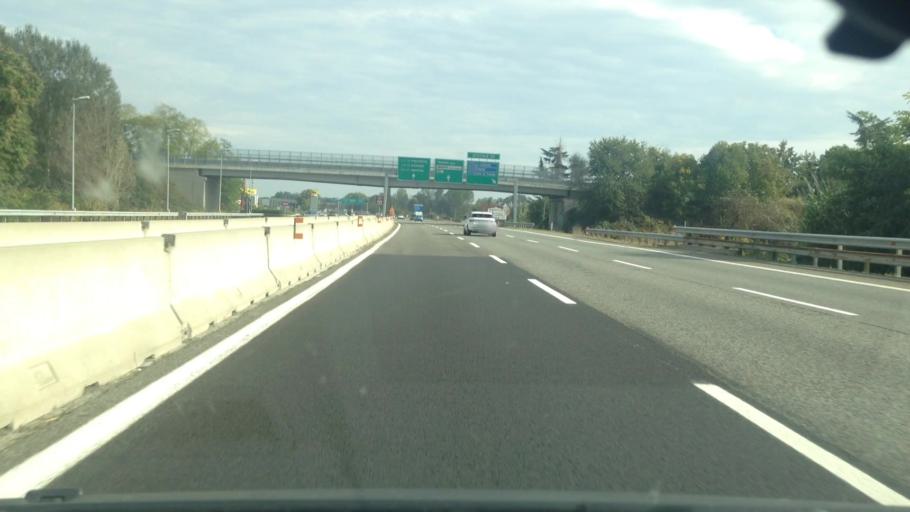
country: IT
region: Piedmont
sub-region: Provincia di Torino
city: Tagliaferro
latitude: 44.9766
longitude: 7.6544
